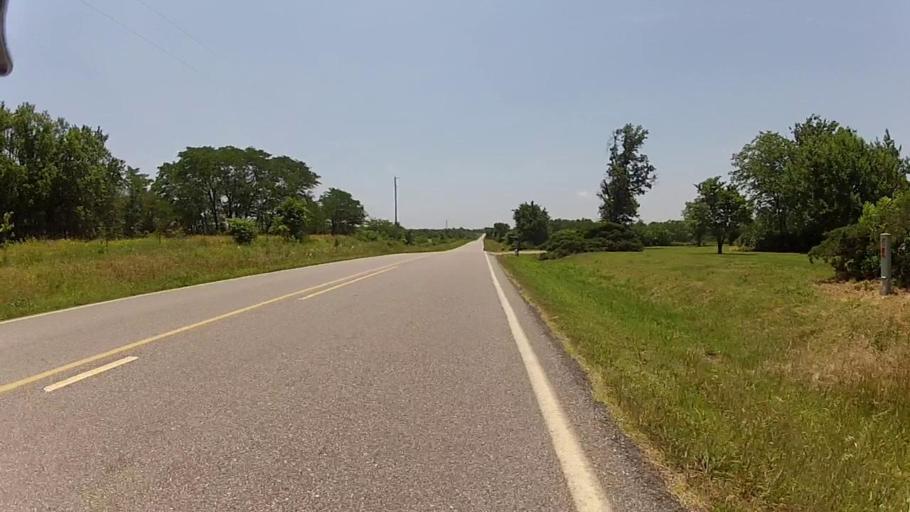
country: US
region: Kansas
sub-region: Montgomery County
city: Cherryvale
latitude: 37.2348
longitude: -95.5377
